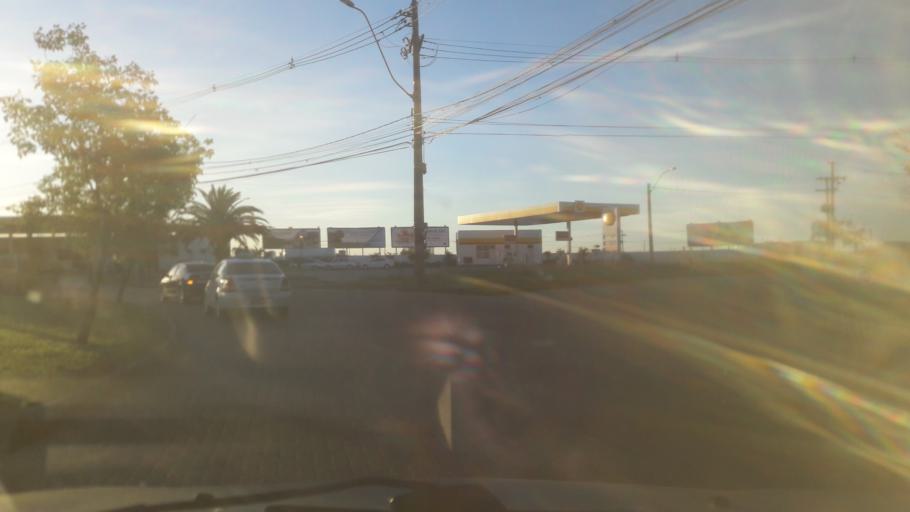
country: BR
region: Rio Grande do Sul
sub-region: Canoas
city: Canoas
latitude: -29.9873
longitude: -51.1713
